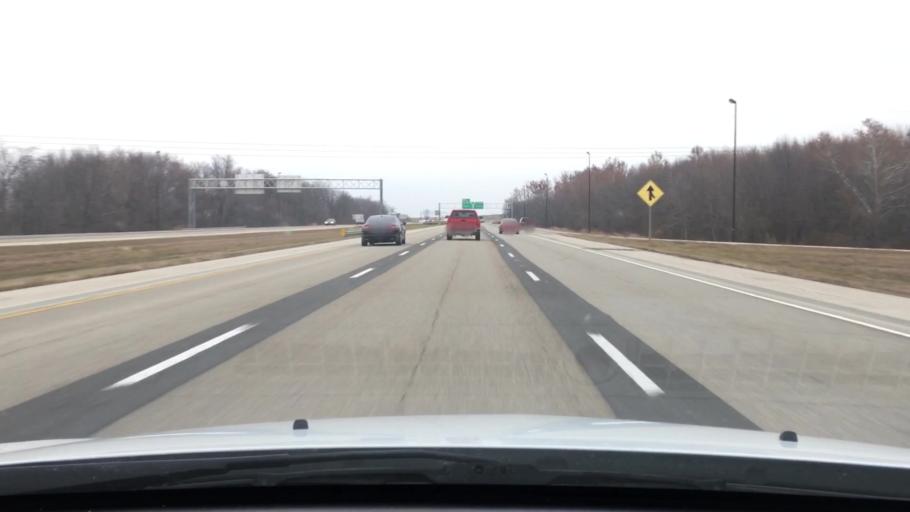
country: US
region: Illinois
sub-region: Logan County
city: Lincoln
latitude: 40.1639
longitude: -89.4176
